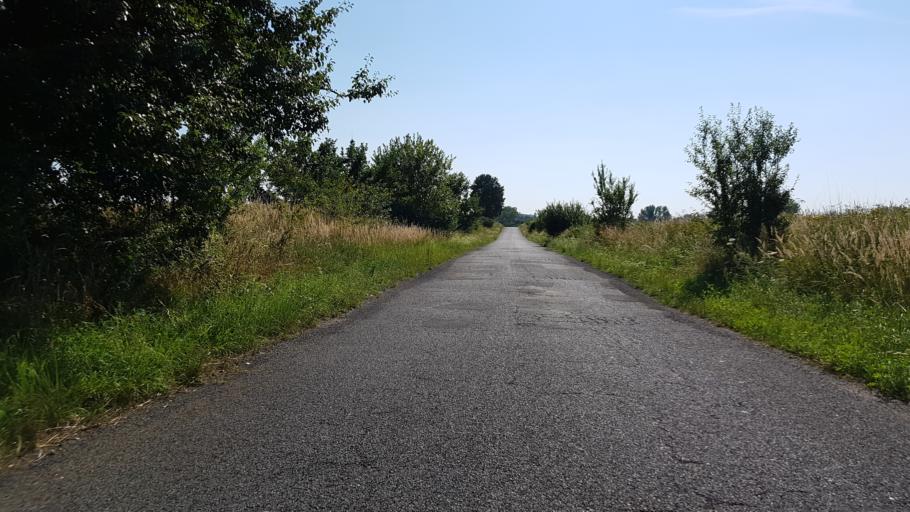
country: PL
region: West Pomeranian Voivodeship
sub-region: Powiat gryfinski
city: Gryfino
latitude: 53.1532
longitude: 14.5183
